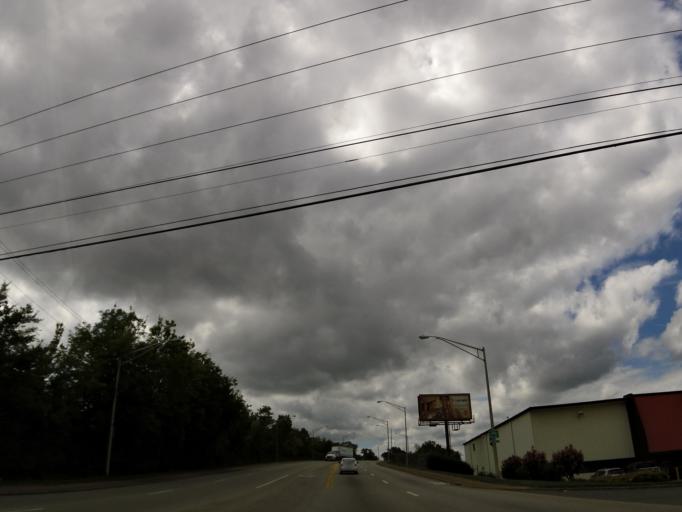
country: US
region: Tennessee
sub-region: Hamilton County
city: Chattanooga
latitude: 35.0242
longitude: -85.3118
